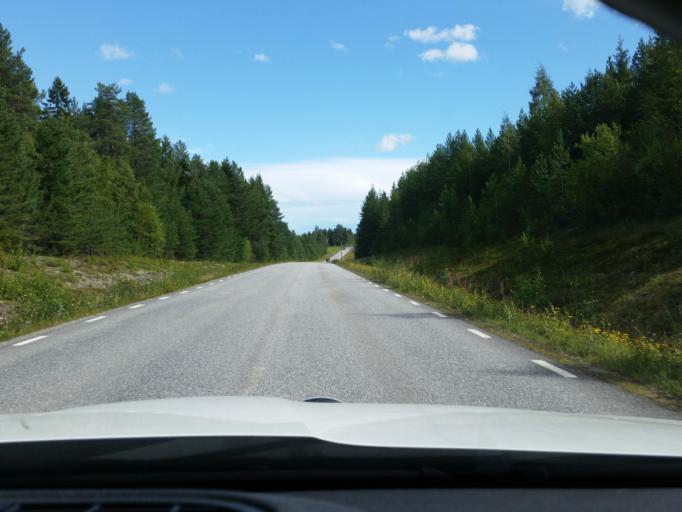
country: SE
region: Norrbotten
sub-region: Pitea Kommun
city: Hortlax
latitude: 65.2748
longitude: 21.3692
